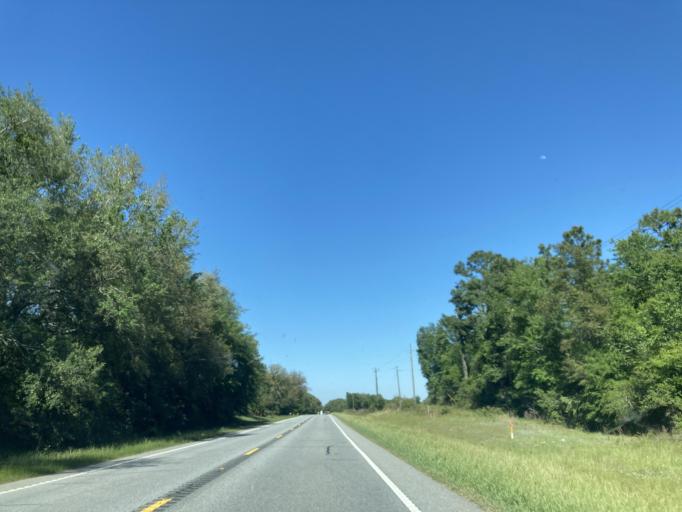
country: US
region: Georgia
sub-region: Baker County
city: Newton
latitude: 31.1973
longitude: -84.5078
